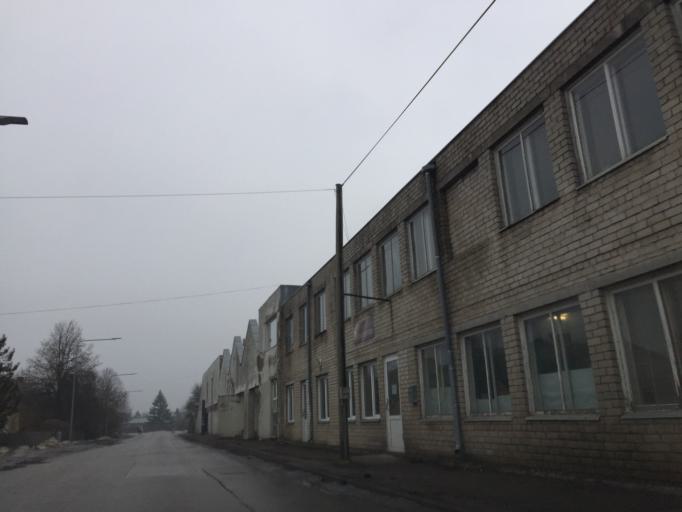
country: EE
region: Saare
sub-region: Kuressaare linn
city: Kuressaare
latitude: 58.2526
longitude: 22.4998
